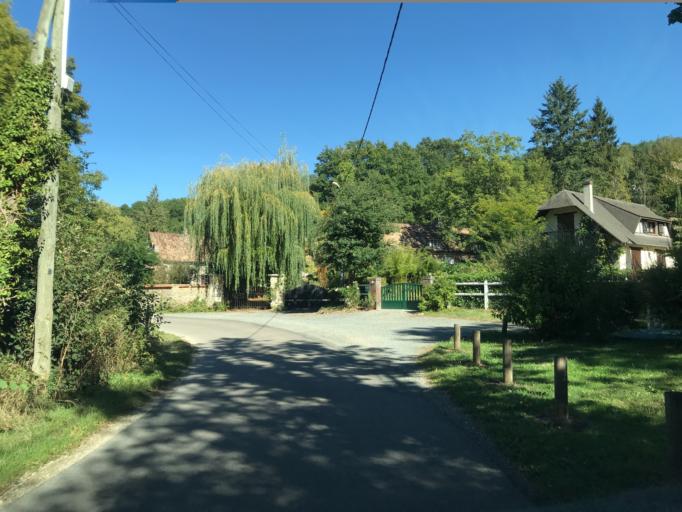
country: FR
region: Haute-Normandie
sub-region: Departement de l'Eure
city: Houlbec-Cocherel
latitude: 49.0994
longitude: 1.3403
